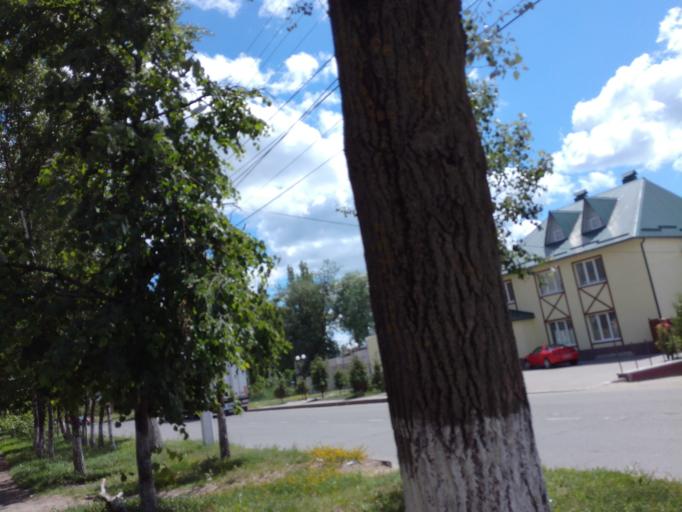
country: RU
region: Kursk
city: Kursk
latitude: 51.7422
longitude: 36.2482
